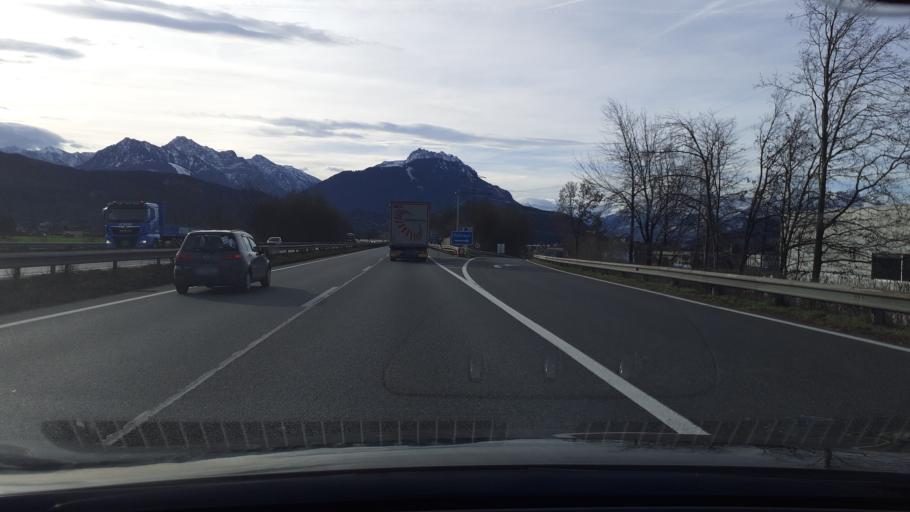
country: AT
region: Vorarlberg
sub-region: Politischer Bezirk Feldkirch
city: Rankweil
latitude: 47.2823
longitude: 9.6241
